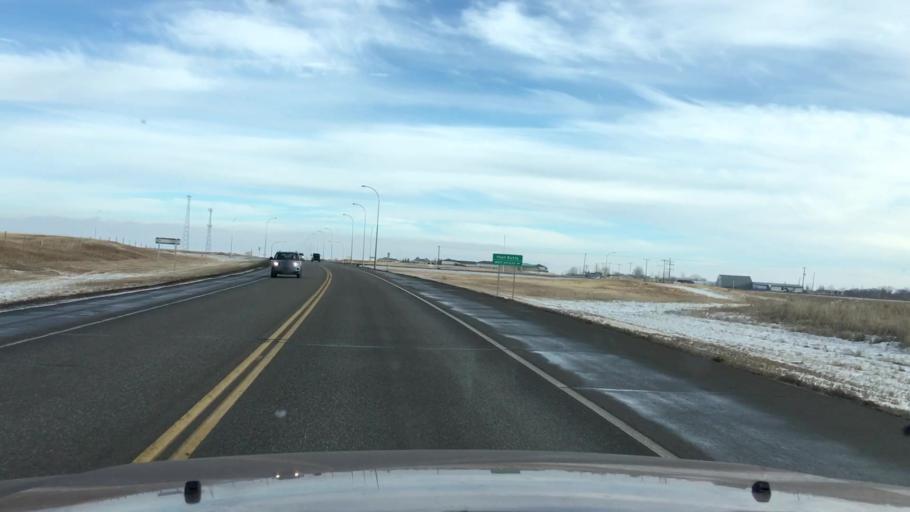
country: CA
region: Saskatchewan
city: Pilot Butte
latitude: 50.4847
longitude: -104.4391
